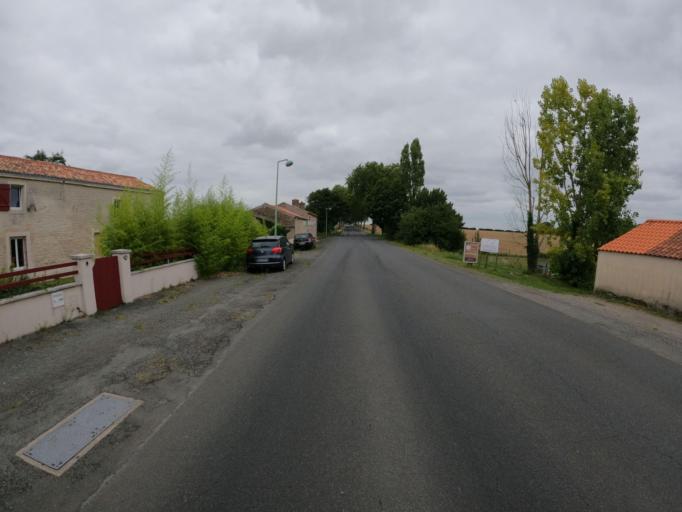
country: FR
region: Pays de la Loire
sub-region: Departement de la Vendee
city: Saint-Martin-sous-Mouzeuil
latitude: 46.5048
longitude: -0.9430
